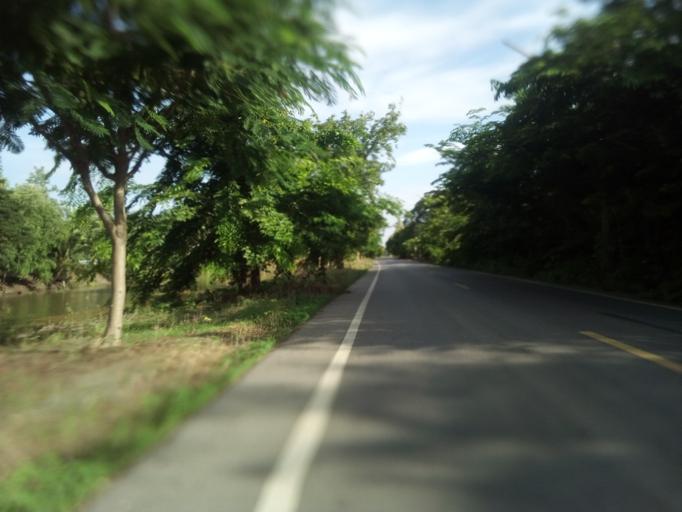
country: TH
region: Pathum Thani
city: Nong Suea
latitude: 14.1228
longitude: 100.8460
